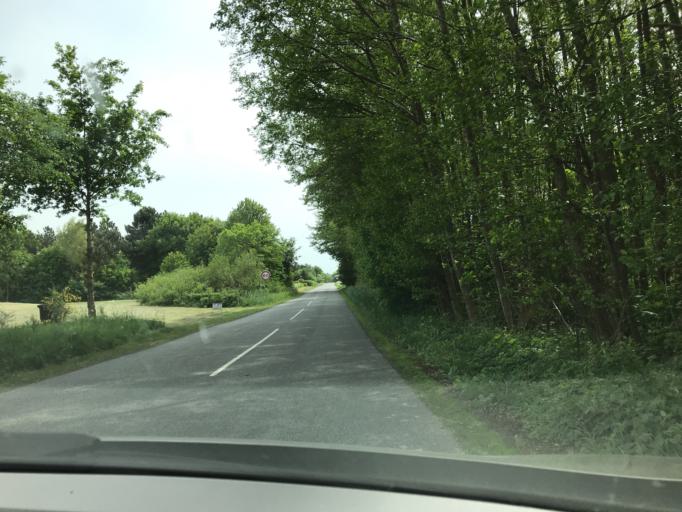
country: DK
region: Central Jutland
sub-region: Norddjurs Kommune
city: Allingabro
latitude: 56.5987
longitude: 10.3120
